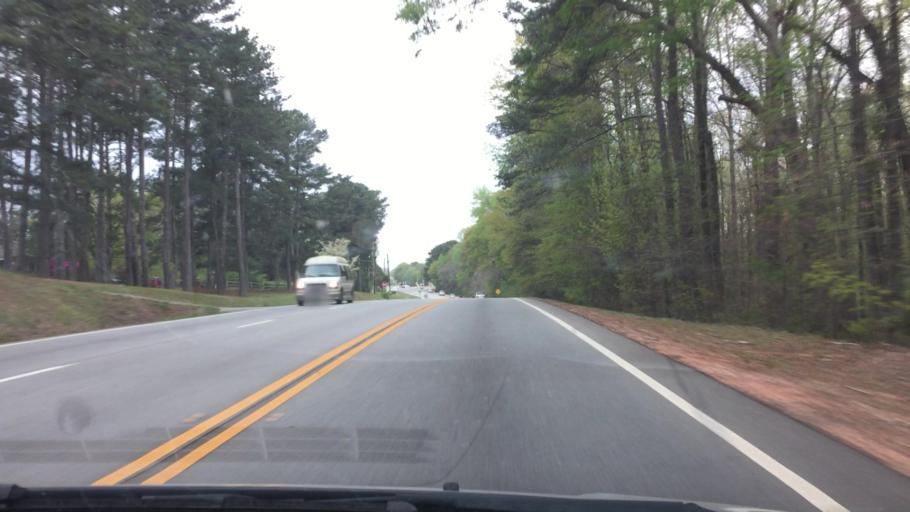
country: US
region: Georgia
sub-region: Henry County
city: Locust Grove
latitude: 33.3397
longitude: -84.0982
